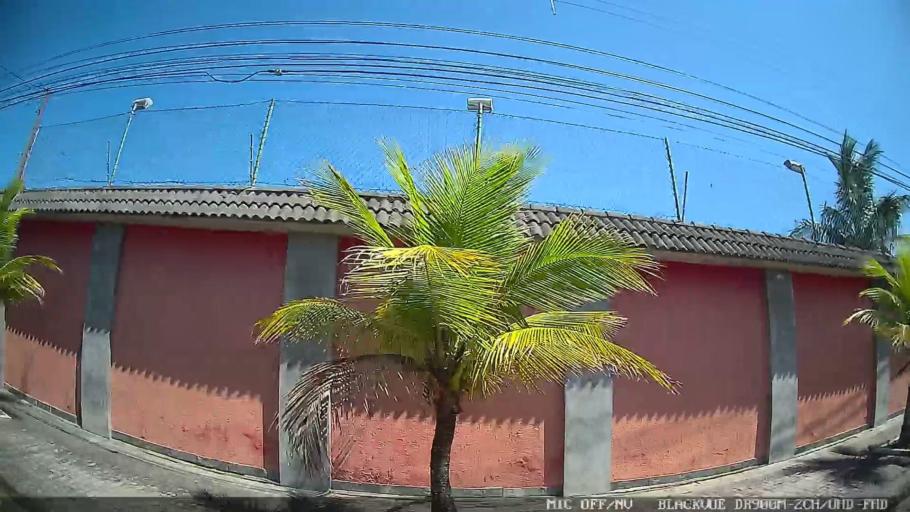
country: BR
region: Sao Paulo
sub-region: Peruibe
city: Peruibe
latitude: -24.3004
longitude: -46.9771
